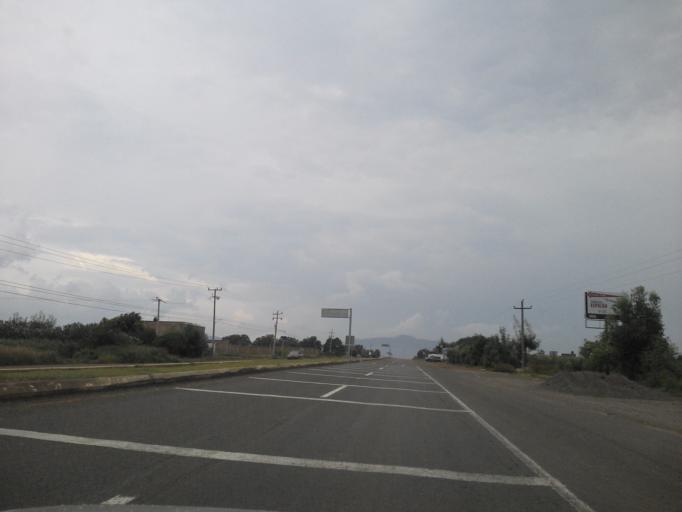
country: MX
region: Jalisco
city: San Jose de Gracia
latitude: 20.7312
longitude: -102.4874
